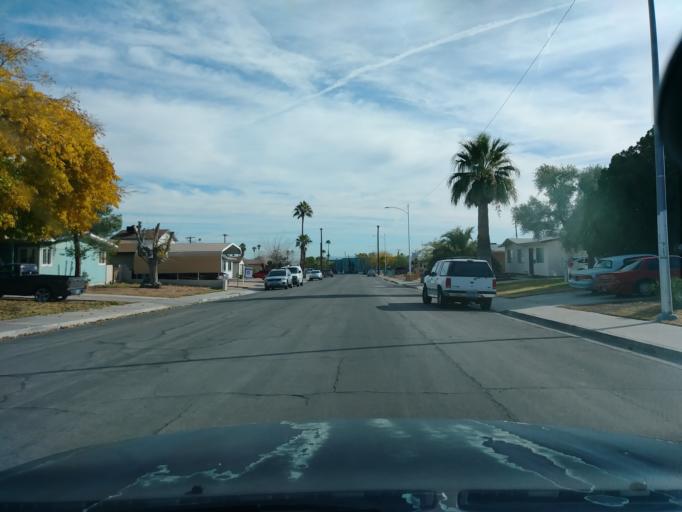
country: US
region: Nevada
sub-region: Clark County
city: Spring Valley
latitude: 36.1613
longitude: -115.2389
